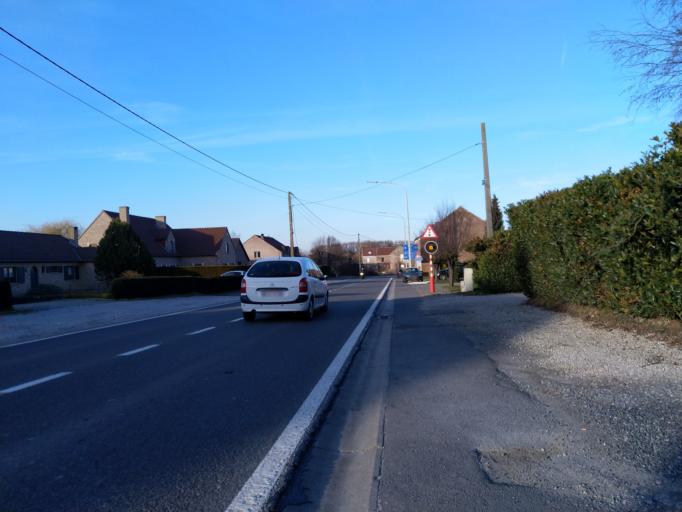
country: BE
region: Wallonia
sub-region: Province du Hainaut
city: Frameries
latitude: 50.4011
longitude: 3.9170
